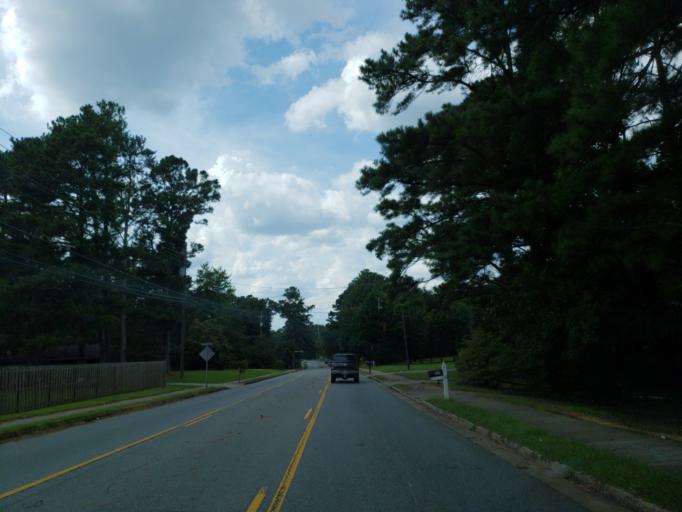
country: US
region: Georgia
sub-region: Cobb County
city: Acworth
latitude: 34.0704
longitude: -84.6322
